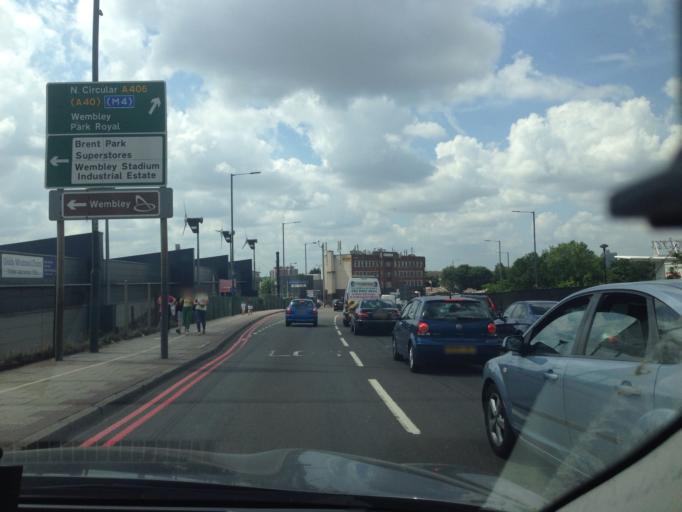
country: GB
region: England
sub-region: Greater London
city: Wembley
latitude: 51.5540
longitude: -0.2534
